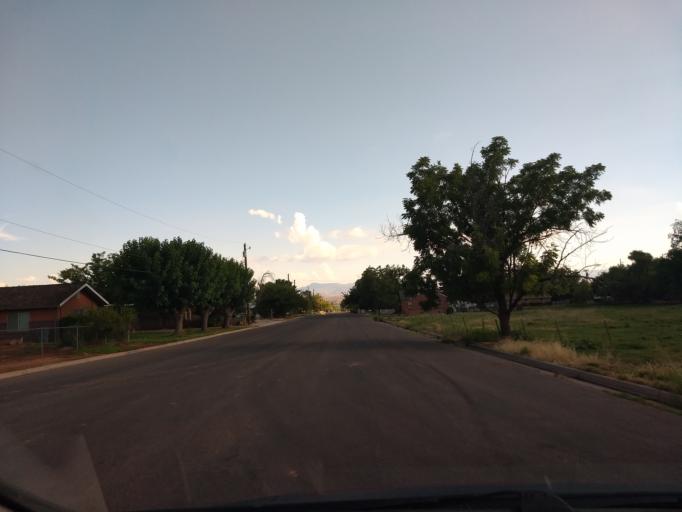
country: US
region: Utah
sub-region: Washington County
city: Washington
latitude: 37.1371
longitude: -113.5082
